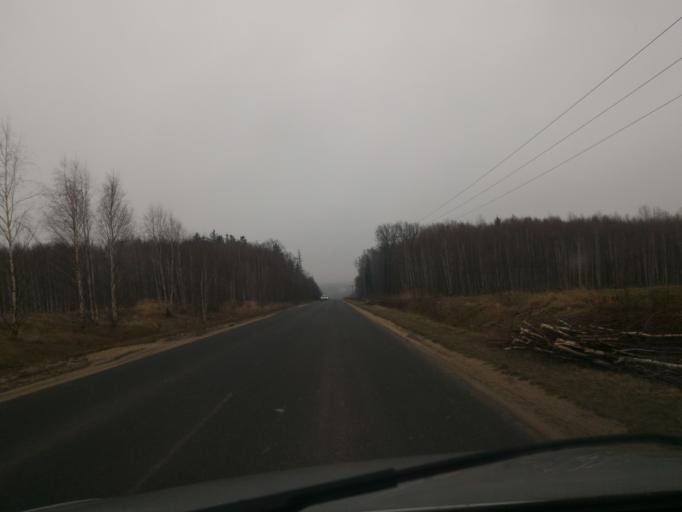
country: PL
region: Lower Silesian Voivodeship
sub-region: Powiat zgorzelecki
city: Bogatynia
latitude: 50.8751
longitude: 14.9119
